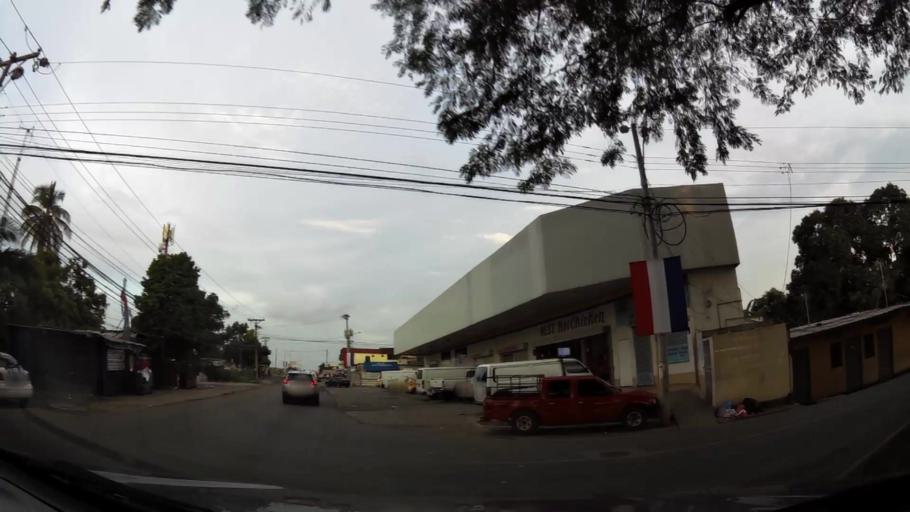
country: PA
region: Panama
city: Tocumen
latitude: 9.0863
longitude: -79.3859
